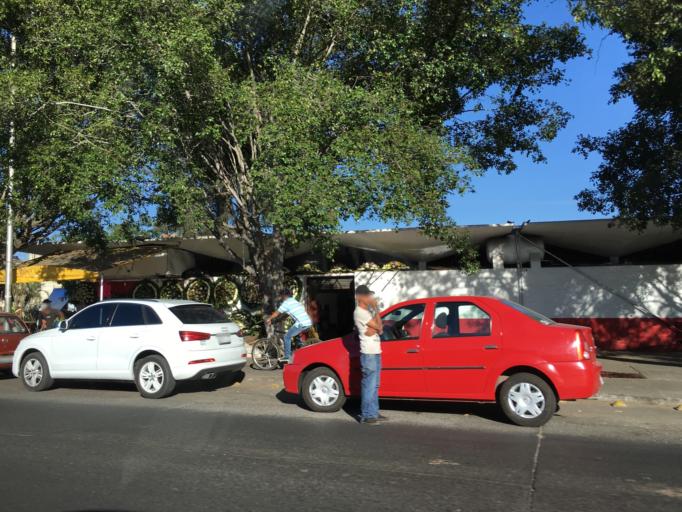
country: MX
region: Jalisco
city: Guadalajara
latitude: 20.6900
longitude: -103.3538
